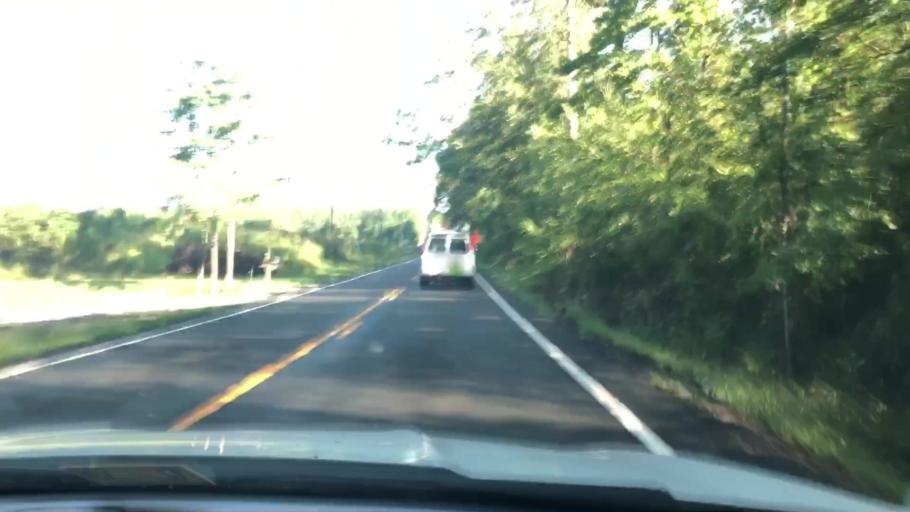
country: US
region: Virginia
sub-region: King William County
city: West Point
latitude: 37.4640
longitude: -76.8427
